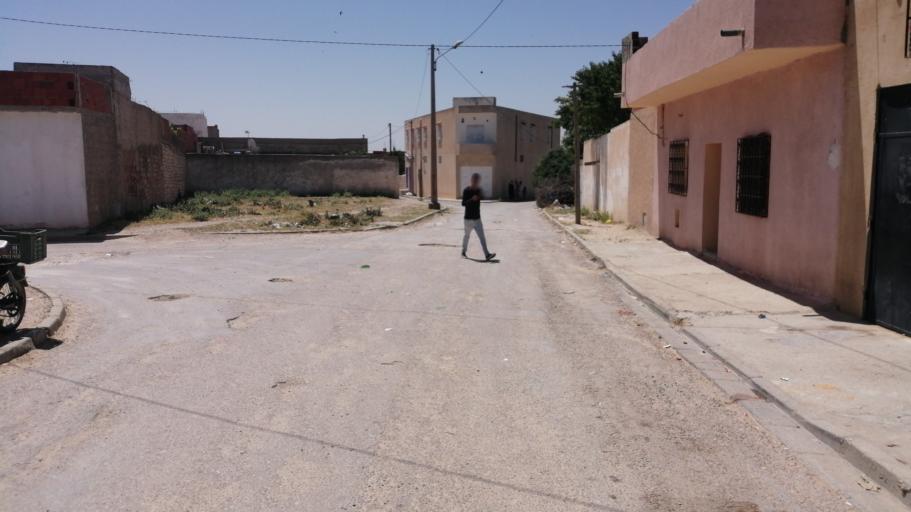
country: TN
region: Silyanah
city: Maktar
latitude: 35.8514
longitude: 9.2039
